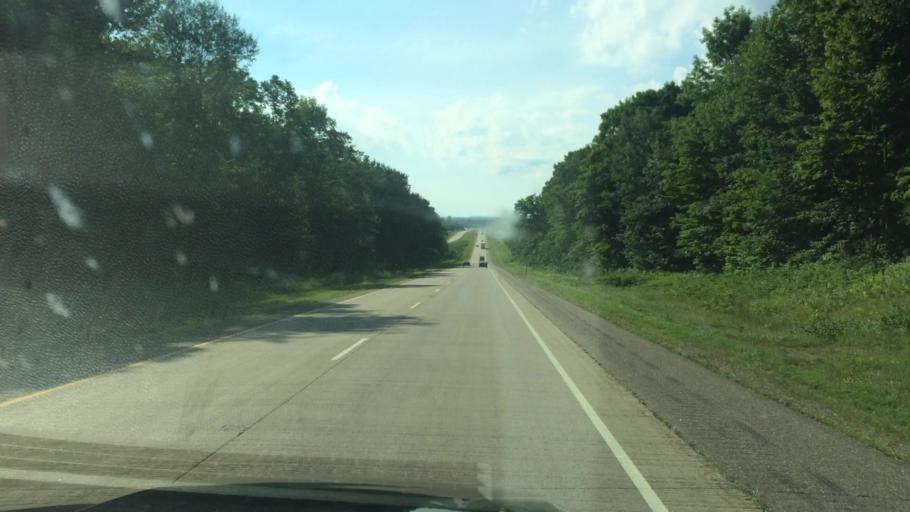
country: US
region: Wisconsin
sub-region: Shawano County
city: Wittenberg
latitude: 44.8183
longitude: -89.0525
